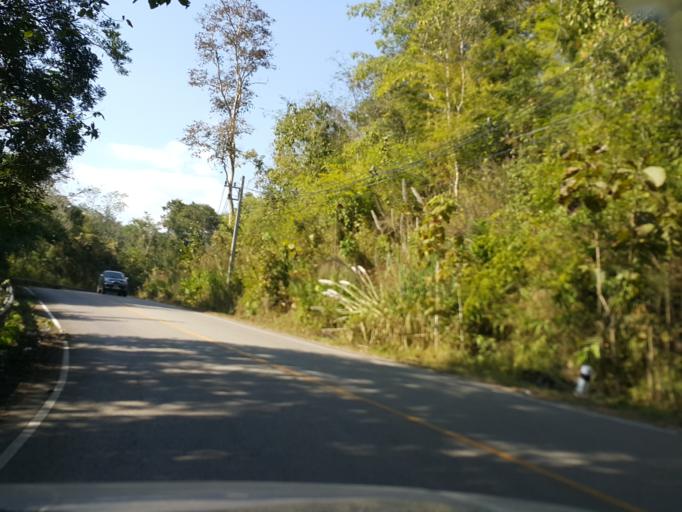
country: TH
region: Chiang Mai
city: Mae Wang
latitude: 18.6337
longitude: 98.7059
